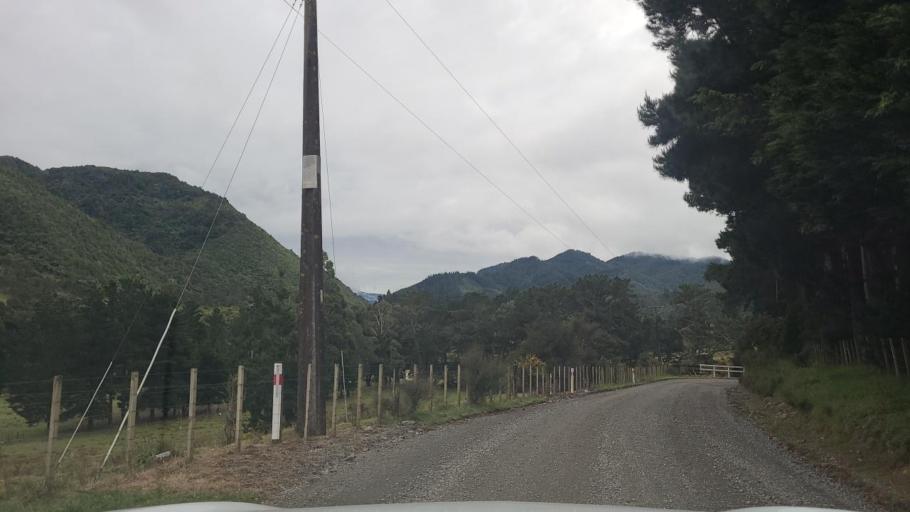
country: NZ
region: Wellington
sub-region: Masterton District
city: Masterton
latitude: -41.0292
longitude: 175.3972
